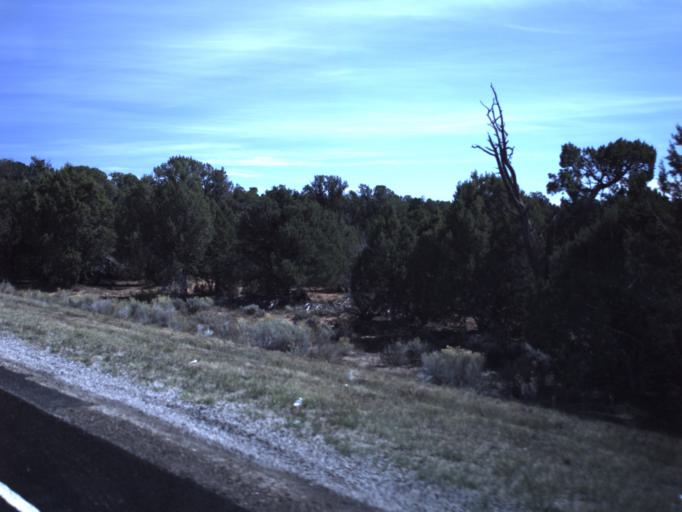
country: US
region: Utah
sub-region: San Juan County
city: Monticello
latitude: 37.8397
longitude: -109.1229
